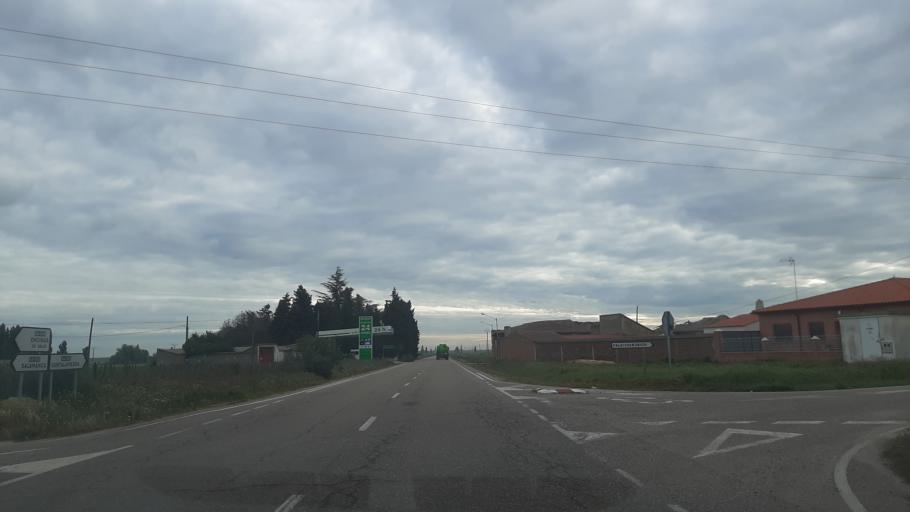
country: ES
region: Castille and Leon
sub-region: Provincia de Salamanca
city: Villaflores
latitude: 41.0829
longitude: -5.2301
